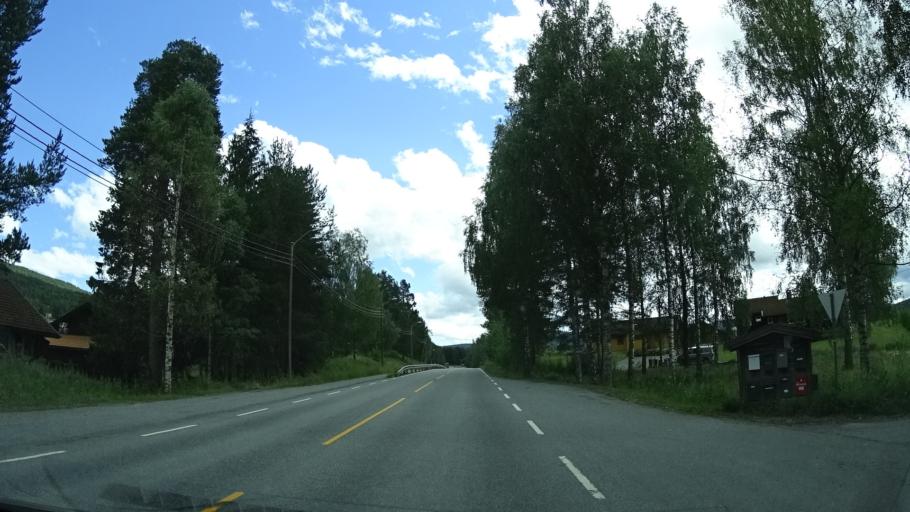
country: NO
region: Buskerud
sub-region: Krodsherad
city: Noresund
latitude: 60.1841
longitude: 9.6157
